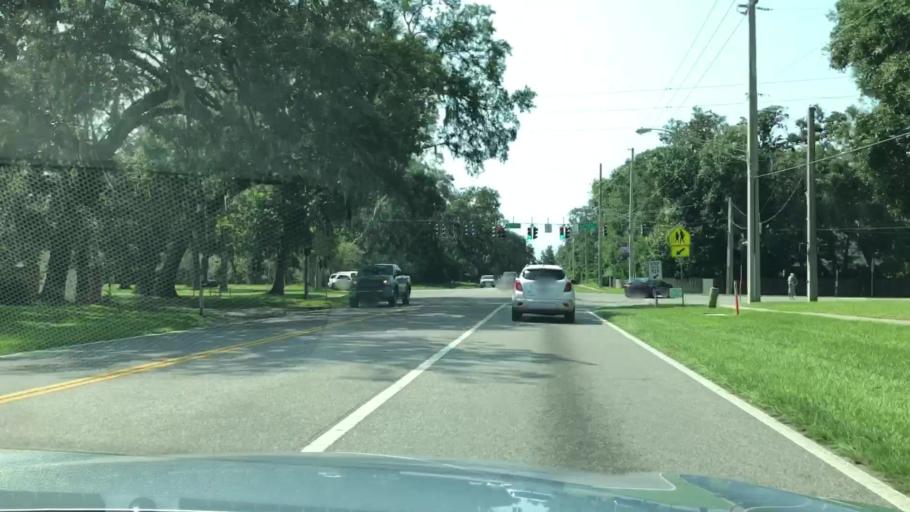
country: US
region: Florida
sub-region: Duval County
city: Neptune Beach
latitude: 30.3156
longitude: -81.4078
